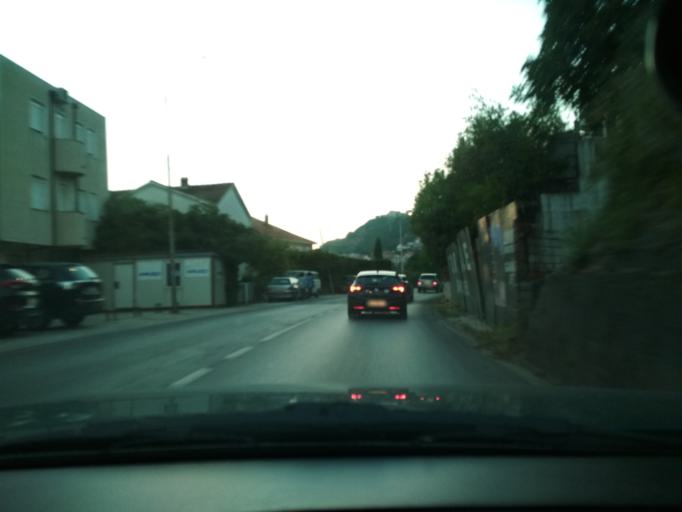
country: ME
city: Igalo
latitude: 42.4586
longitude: 18.5222
